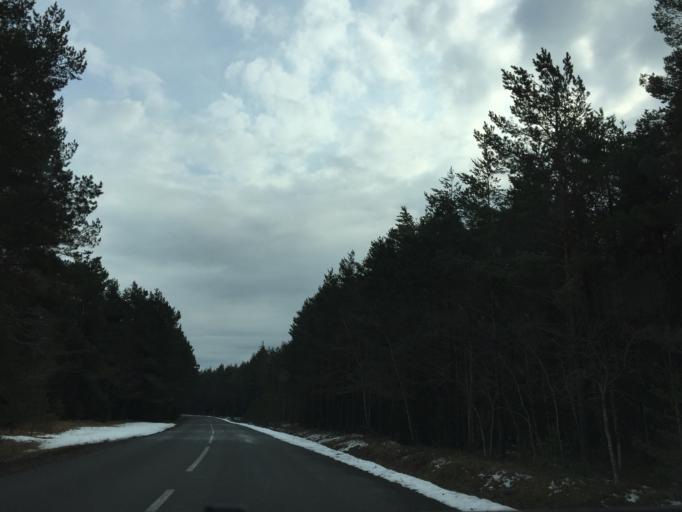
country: EE
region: Saare
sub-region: Kuressaare linn
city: Kuressaare
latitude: 58.4473
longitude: 22.0528
